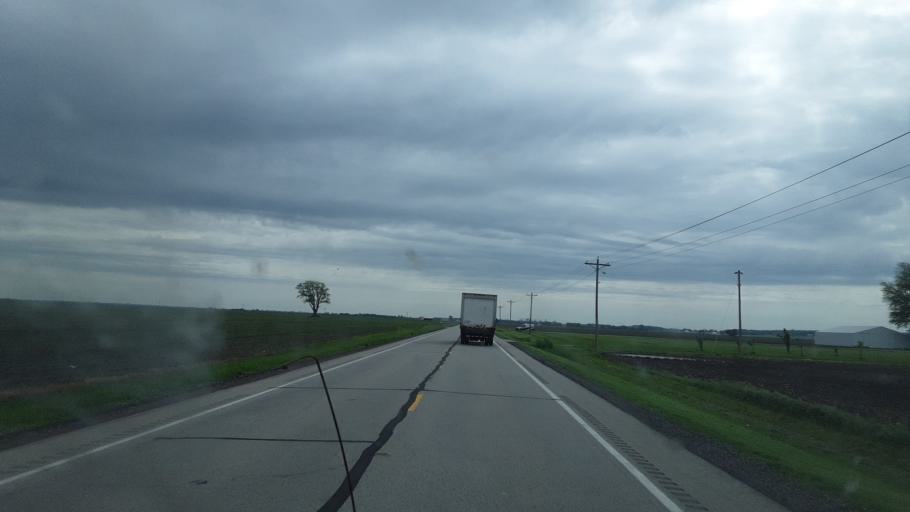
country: US
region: Illinois
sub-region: Mason County
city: Mason City
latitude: 40.3046
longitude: -89.7238
